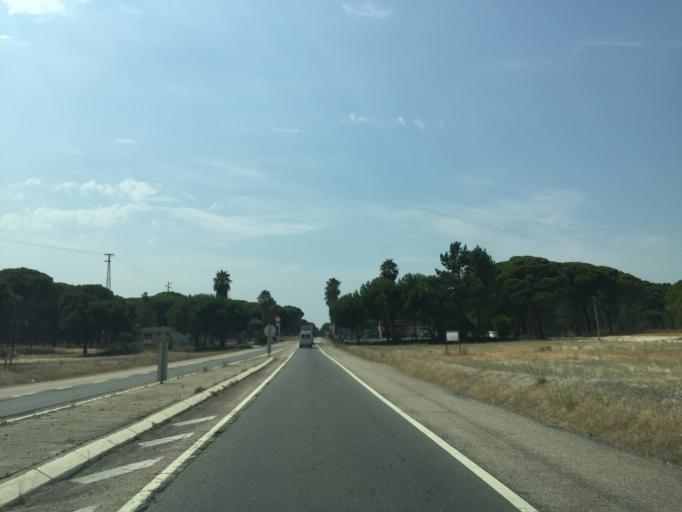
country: PT
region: Setubal
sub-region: Alcacer do Sal
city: Alcacer do Sal
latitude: 38.3095
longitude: -8.5296
